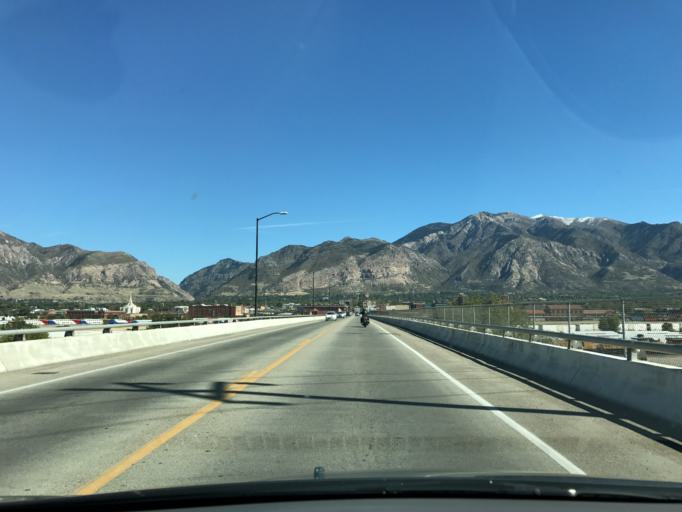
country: US
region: Utah
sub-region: Weber County
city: Ogden
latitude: 41.2229
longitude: -111.9872
